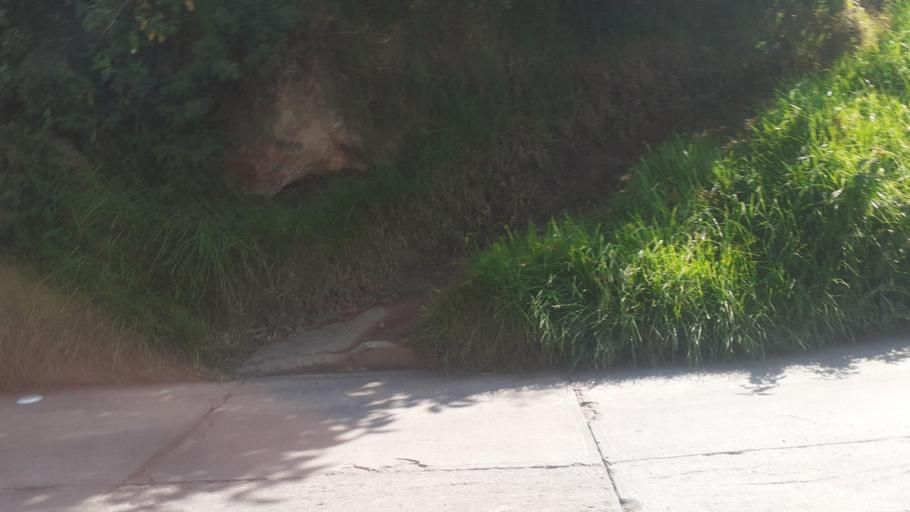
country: GT
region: Quetzaltenango
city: Cantel
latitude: 14.8150
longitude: -91.4510
